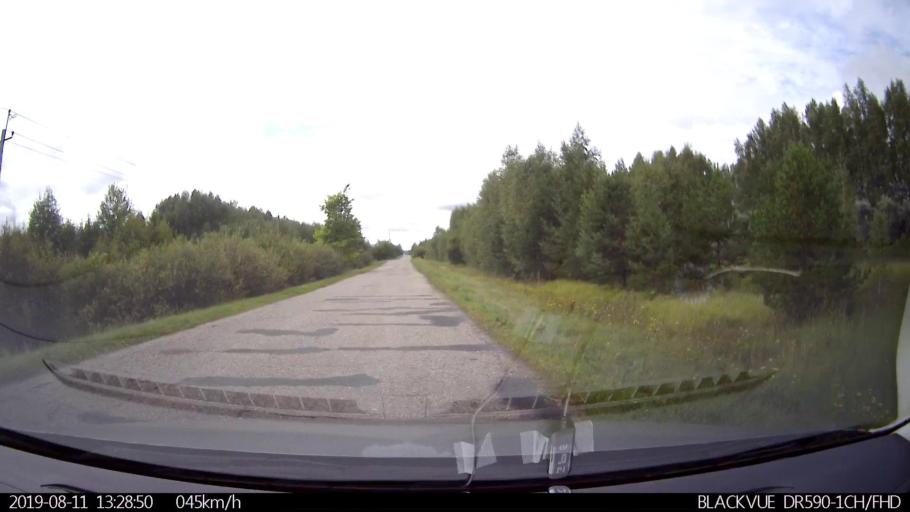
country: RU
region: Ulyanovsk
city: Ignatovka
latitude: 53.8594
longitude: 47.6213
